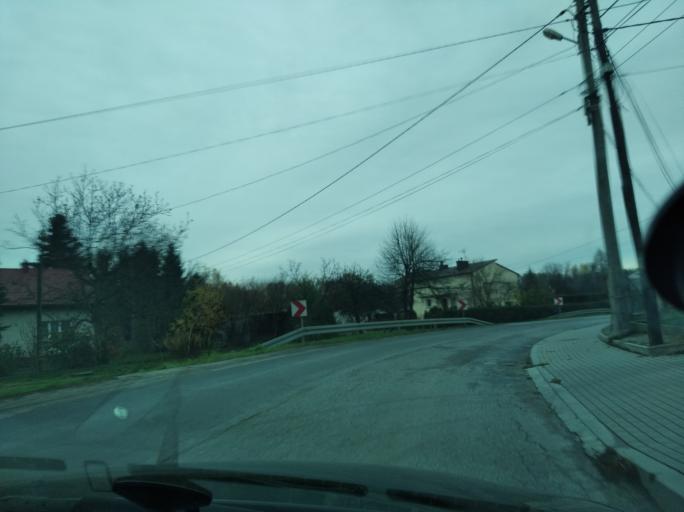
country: PL
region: Subcarpathian Voivodeship
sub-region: Powiat lancucki
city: Krzemienica
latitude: 50.0787
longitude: 22.1906
